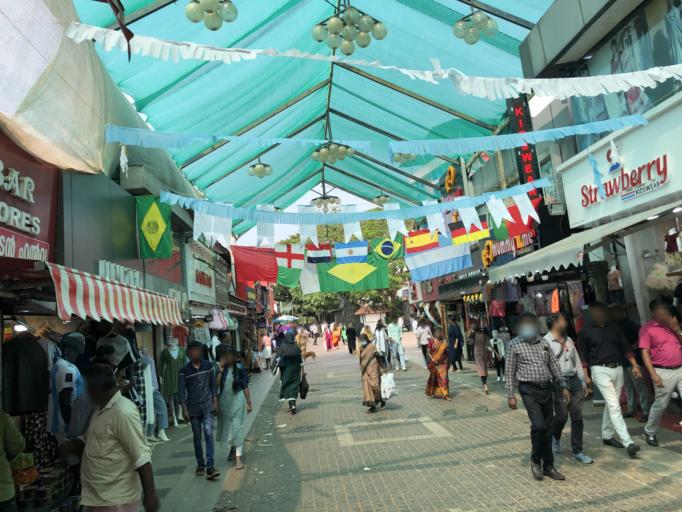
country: IN
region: Kerala
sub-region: Kozhikode
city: Kozhikode
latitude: 11.2519
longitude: 75.7815
